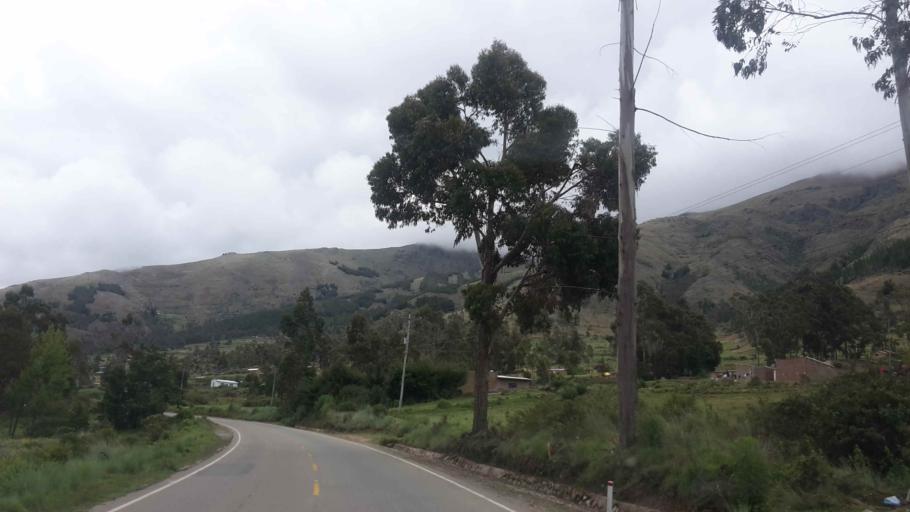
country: BO
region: Cochabamba
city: Arani
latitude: -17.4817
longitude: -65.4796
